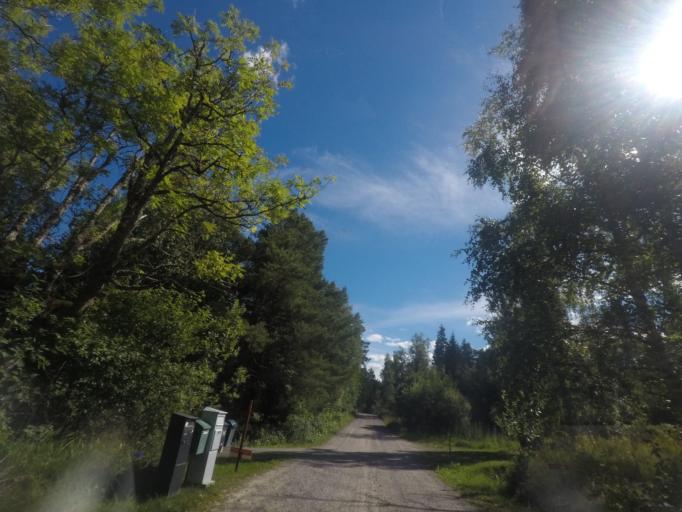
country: SE
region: Stockholm
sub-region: Norrtalje Kommun
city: Arno
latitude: 60.2120
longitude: 18.7305
